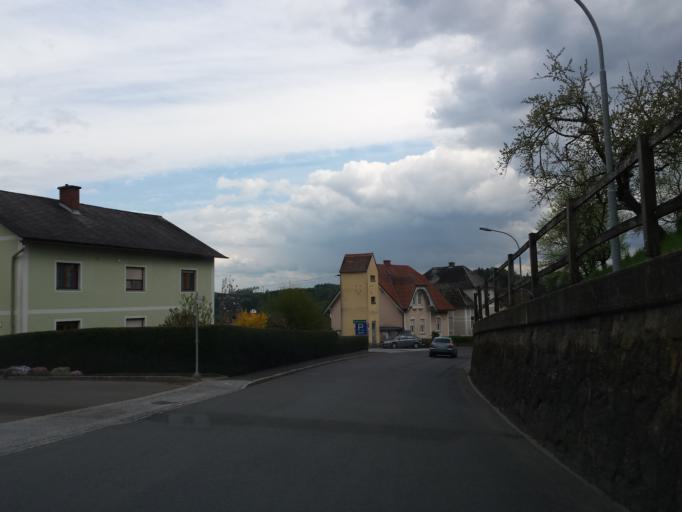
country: AT
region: Styria
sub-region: Politischer Bezirk Suedoststeiermark
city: Riegersburg
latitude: 47.0007
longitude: 15.9371
